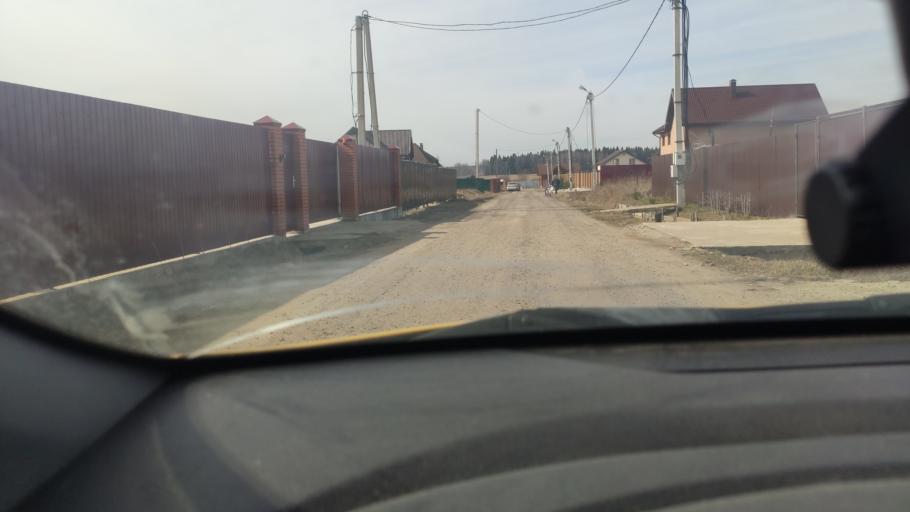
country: RU
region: Moskovskaya
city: Ruza
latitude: 55.7633
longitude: 36.1314
